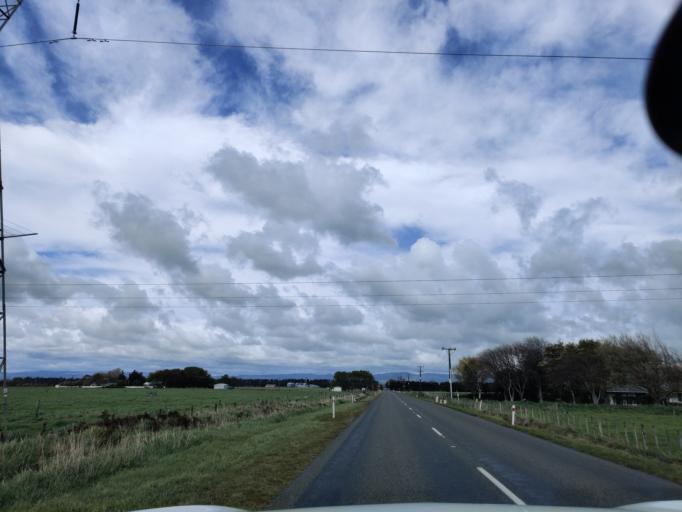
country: NZ
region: Manawatu-Wanganui
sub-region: Palmerston North City
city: Palmerston North
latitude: -40.3319
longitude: 175.5130
